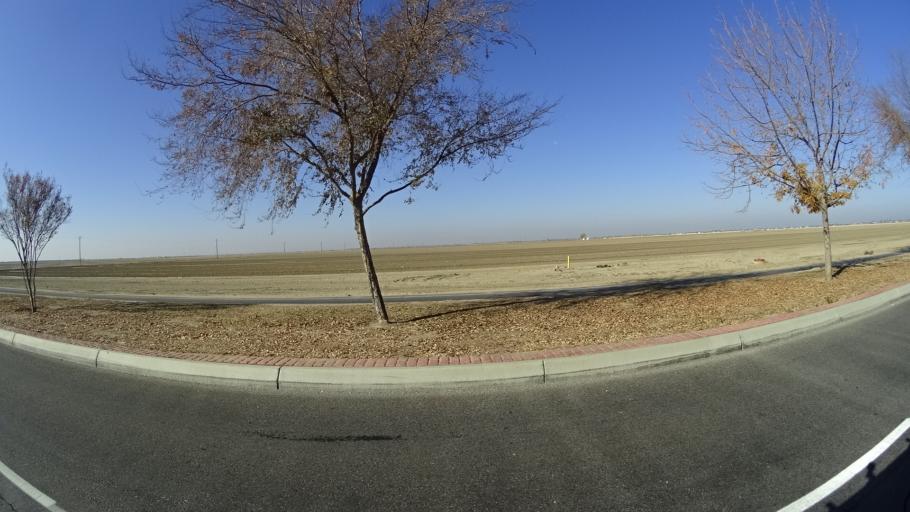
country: US
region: California
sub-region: Kern County
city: Rosedale
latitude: 35.3263
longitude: -119.1456
